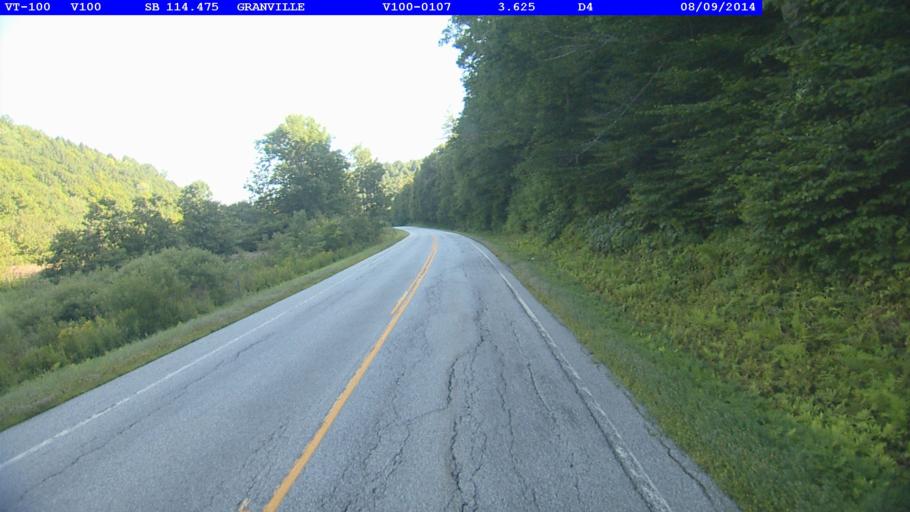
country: US
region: Vermont
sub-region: Orange County
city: Randolph
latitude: 43.9935
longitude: -72.8527
